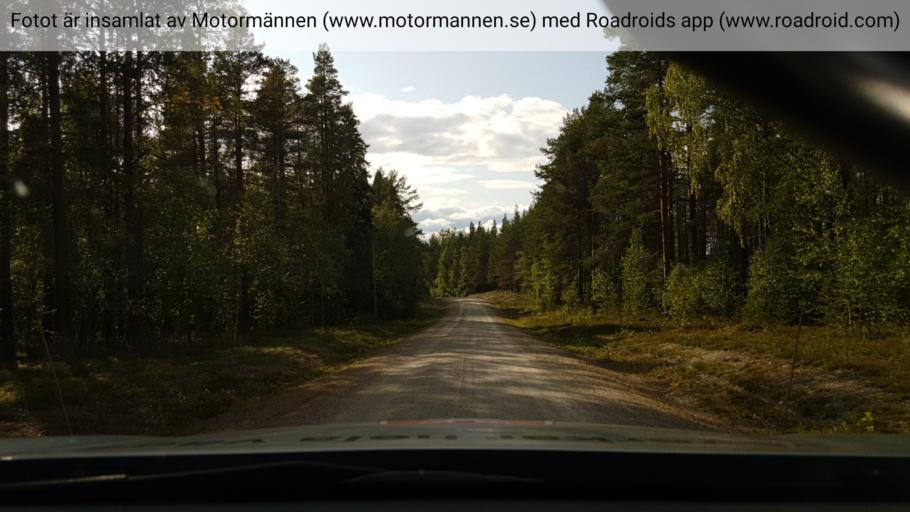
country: SE
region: Vaesterbotten
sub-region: Lycksele Kommun
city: Lycksele
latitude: 64.7228
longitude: 19.0102
